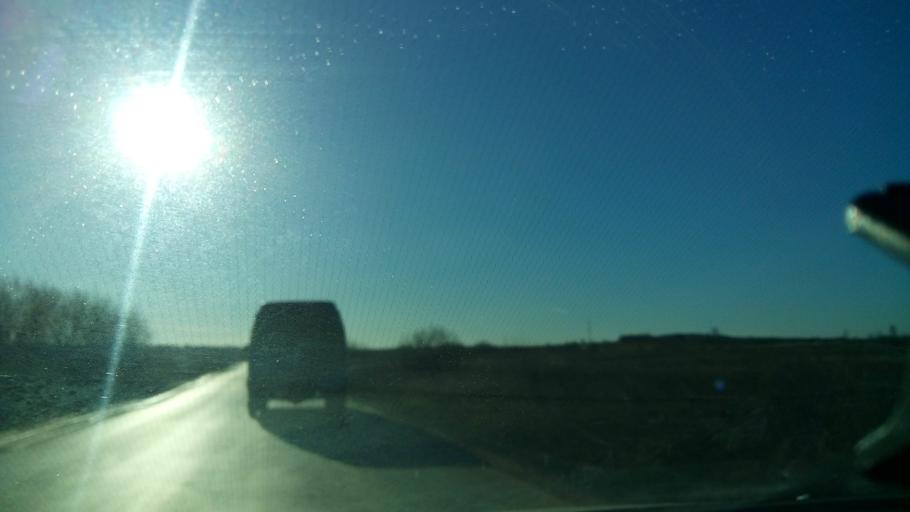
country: RU
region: Sverdlovsk
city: Sovkhoznyy
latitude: 56.7322
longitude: 60.5372
